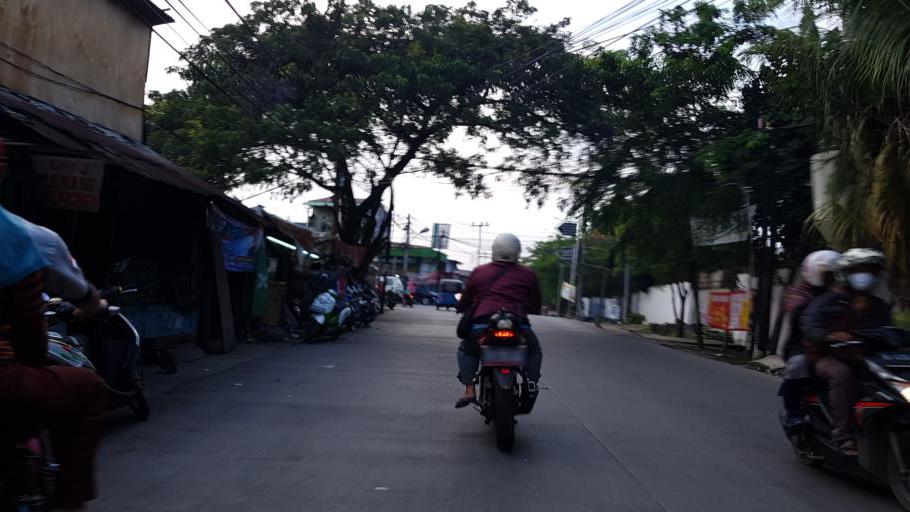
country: ID
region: West Java
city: Teluknaga
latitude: -6.1272
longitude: 106.7391
